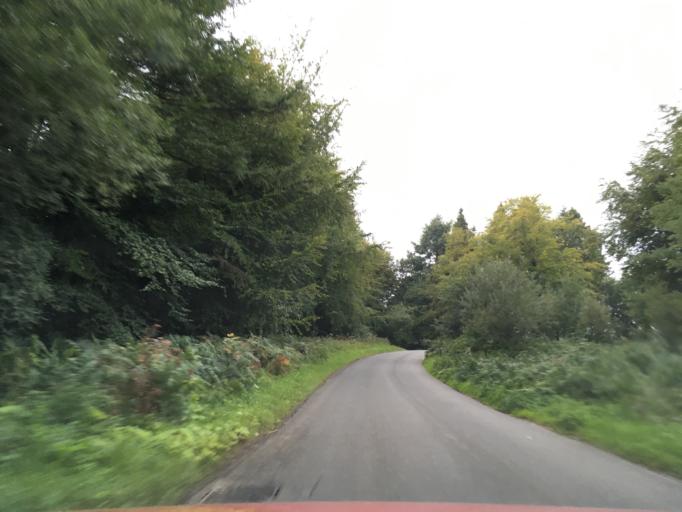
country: GB
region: Wales
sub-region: Newport
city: Llanvaches
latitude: 51.6488
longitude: -2.8356
